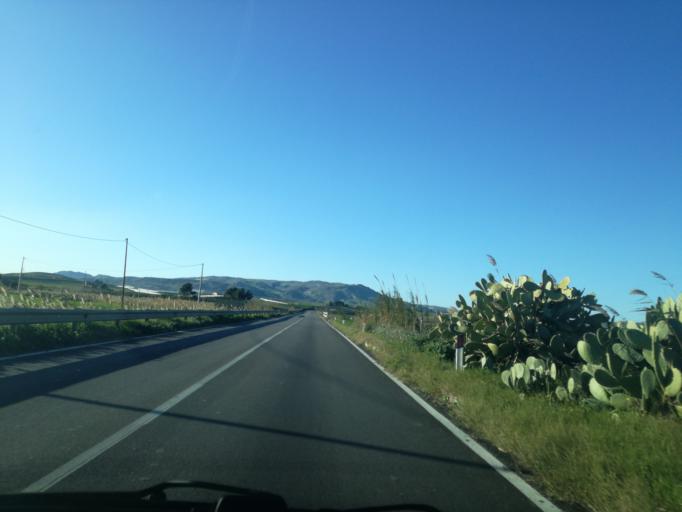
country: IT
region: Sicily
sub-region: Provincia di Caltanissetta
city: Butera
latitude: 37.1208
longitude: 14.1306
